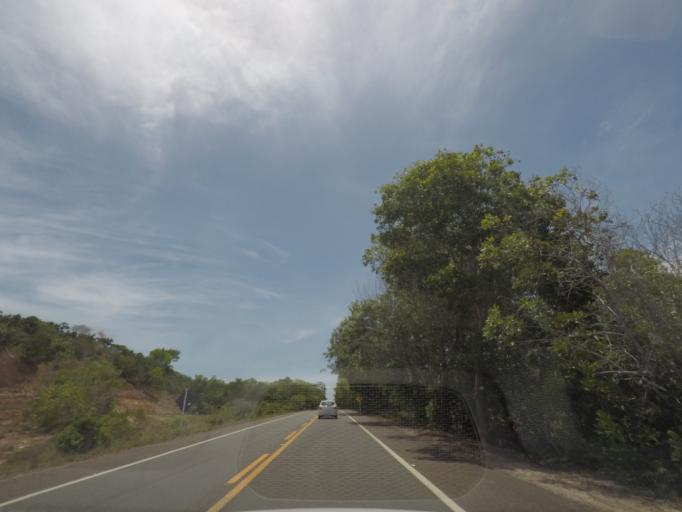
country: BR
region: Bahia
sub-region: Mata De Sao Joao
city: Mata de Sao Joao
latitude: -12.3984
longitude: -37.9199
